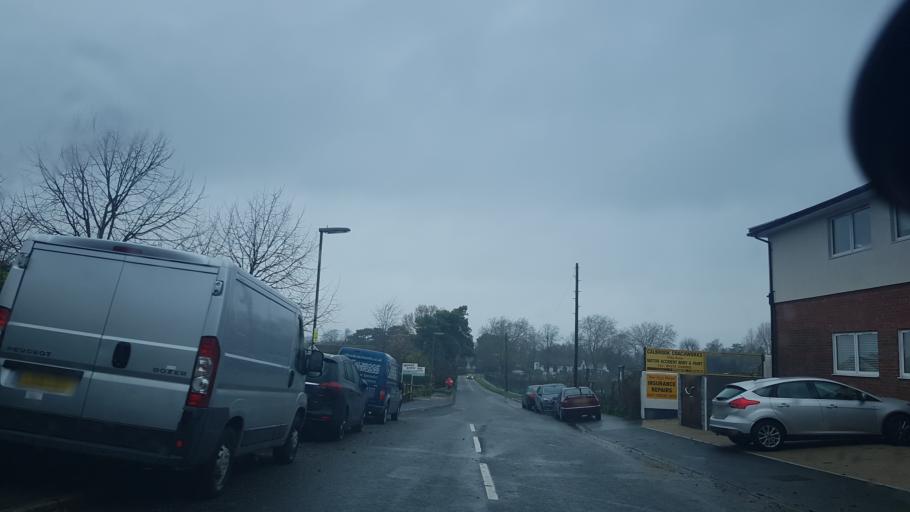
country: GB
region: England
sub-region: Surrey
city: Great Bookham
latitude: 51.2777
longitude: -0.3664
